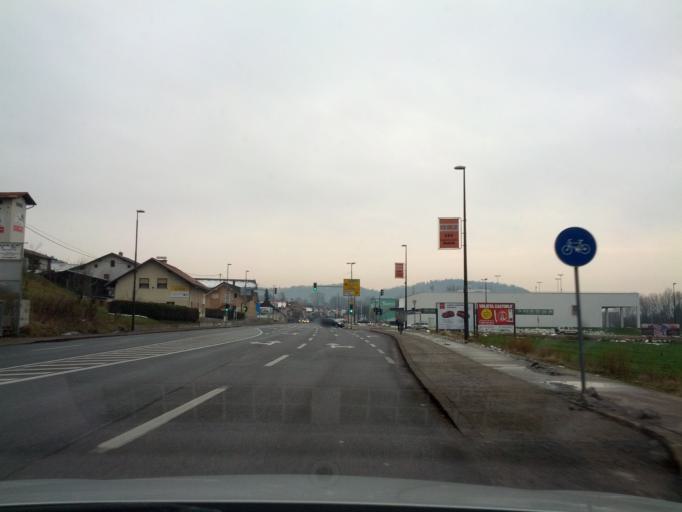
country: SI
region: Skofljica
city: Lavrica
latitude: 46.0265
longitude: 14.5374
